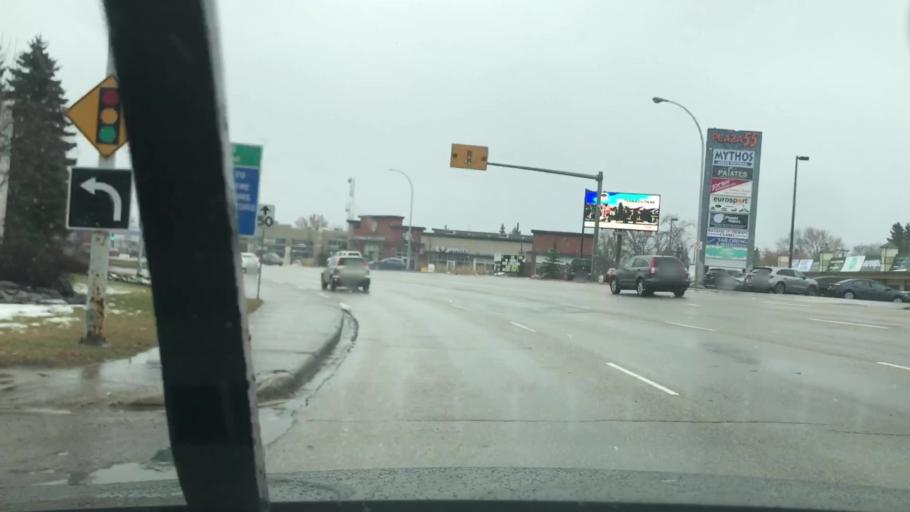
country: CA
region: Alberta
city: Edmonton
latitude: 53.4935
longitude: -113.4976
